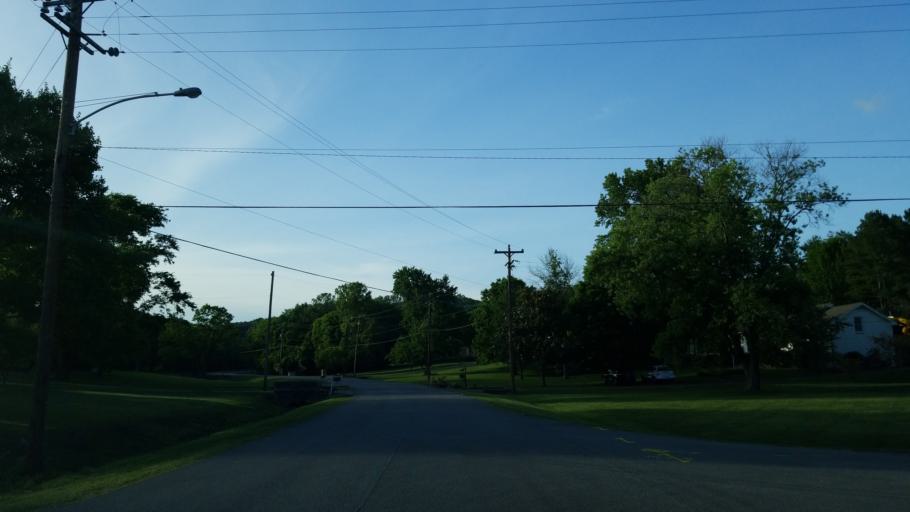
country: US
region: Tennessee
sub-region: Davidson County
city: Forest Hills
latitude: 36.0409
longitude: -86.8449
